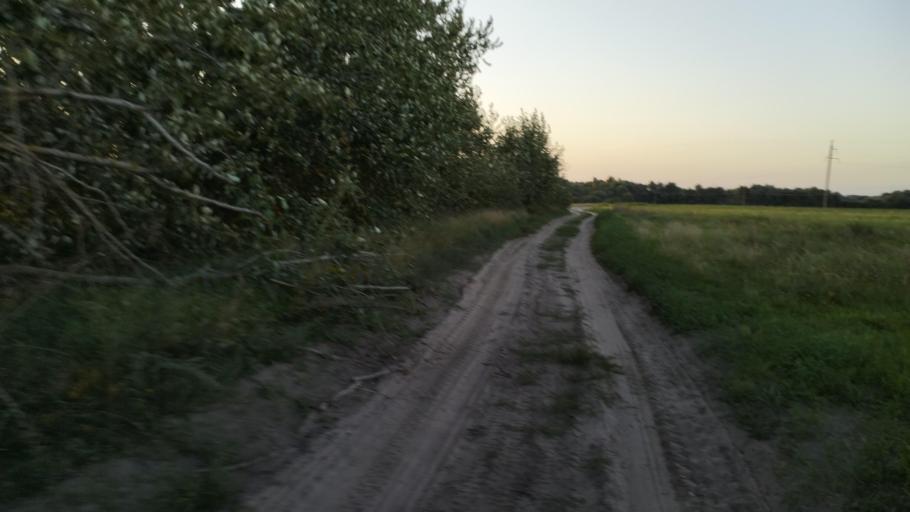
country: BY
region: Brest
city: Davyd-Haradok
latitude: 52.0330
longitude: 27.1934
